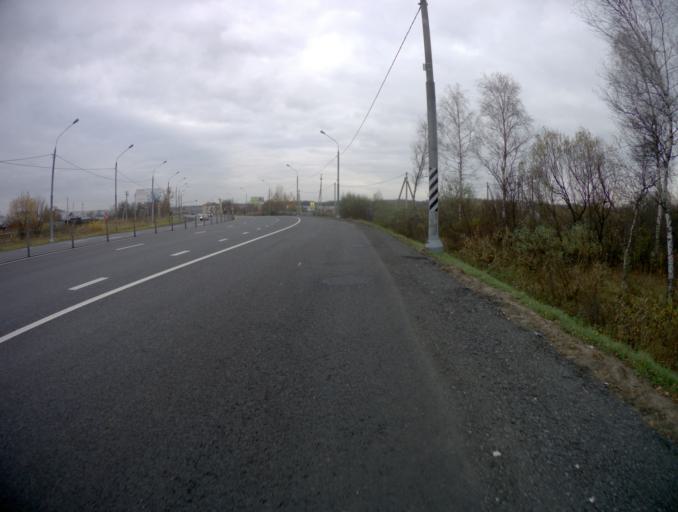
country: RU
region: Moskovskaya
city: Malaya Dubna
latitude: 55.8737
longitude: 38.9636
